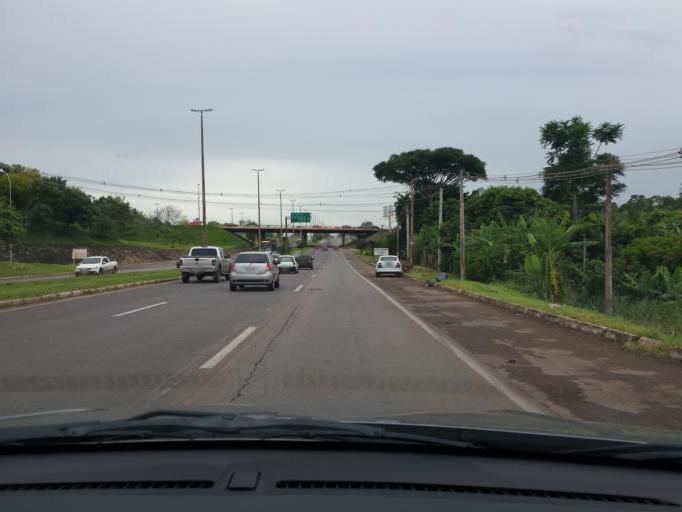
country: BR
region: Federal District
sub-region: Brasilia
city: Brasilia
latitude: -15.8641
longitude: -47.9569
